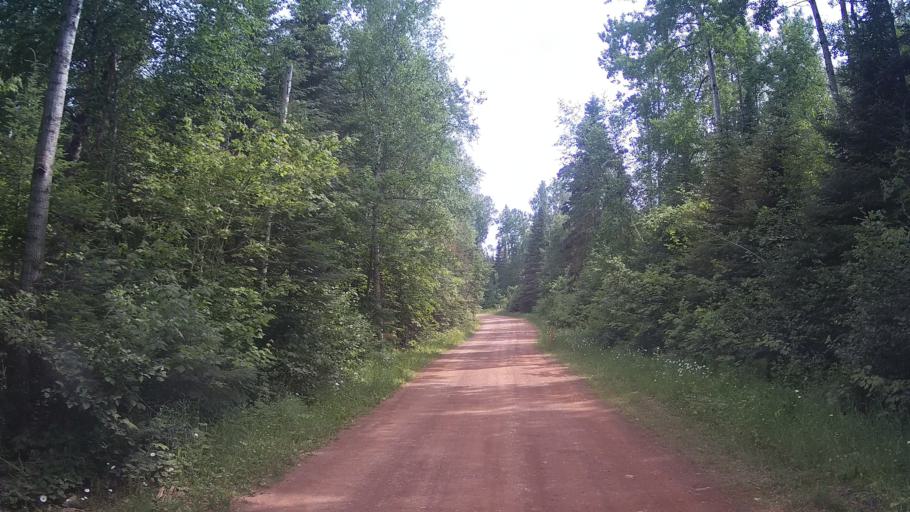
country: CA
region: Ontario
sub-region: Thunder Bay District
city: Thunder Bay
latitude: 48.6731
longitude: -88.6681
